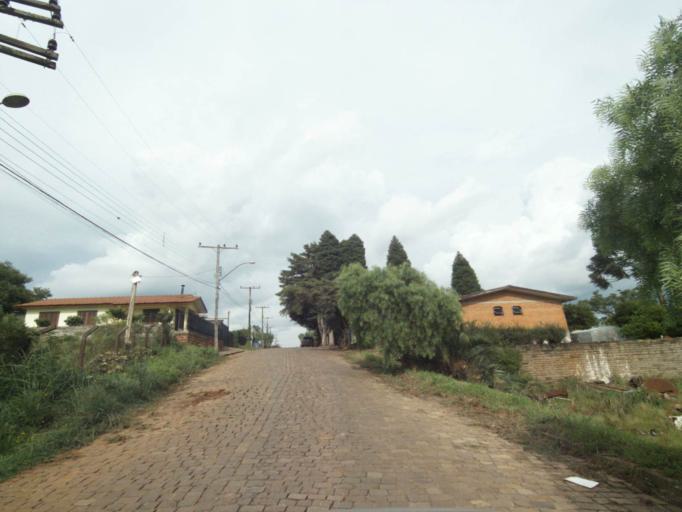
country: BR
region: Rio Grande do Sul
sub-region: Lagoa Vermelha
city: Lagoa Vermelha
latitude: -28.2294
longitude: -51.5061
